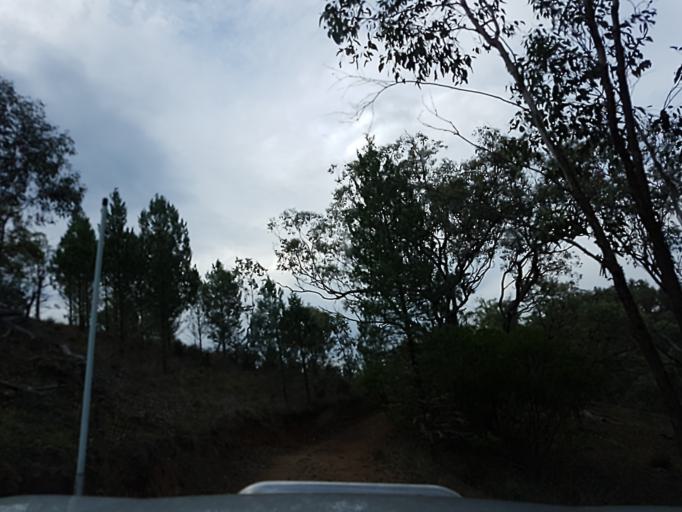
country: AU
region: New South Wales
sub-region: Snowy River
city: Jindabyne
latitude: -36.9564
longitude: 148.3832
